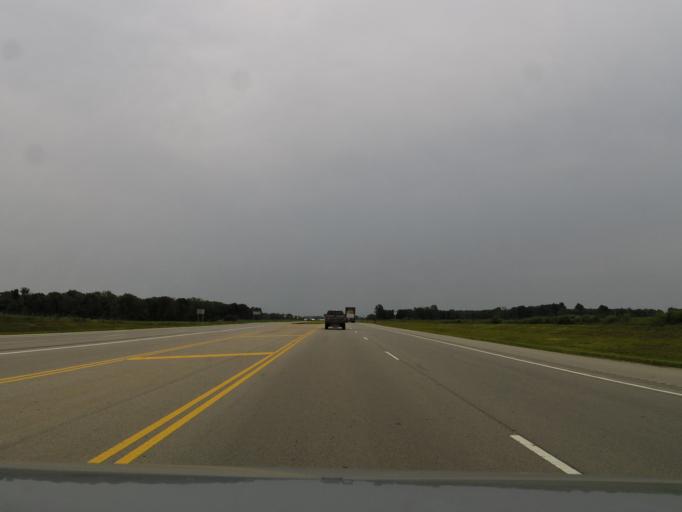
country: US
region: Ohio
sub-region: Clinton County
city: Wilmington
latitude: 39.4640
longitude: -83.8681
